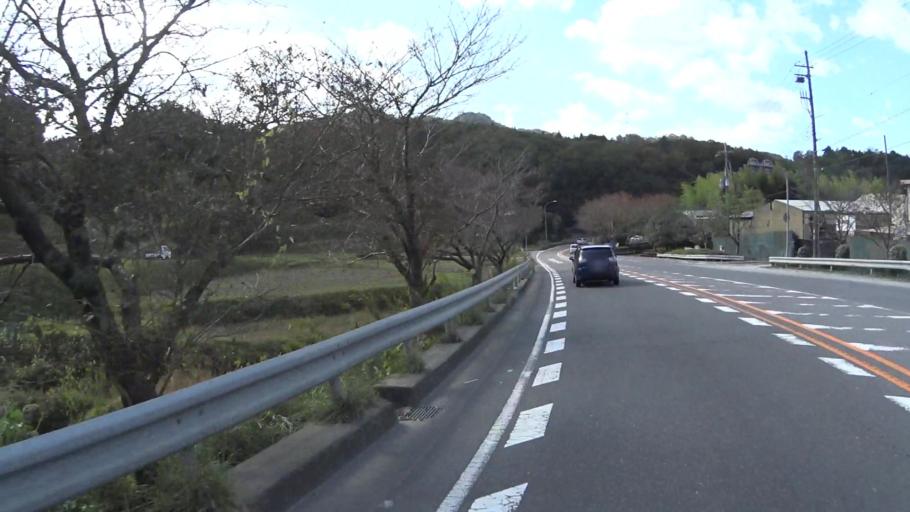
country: JP
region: Kyoto
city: Kameoka
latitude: 34.9920
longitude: 135.6273
